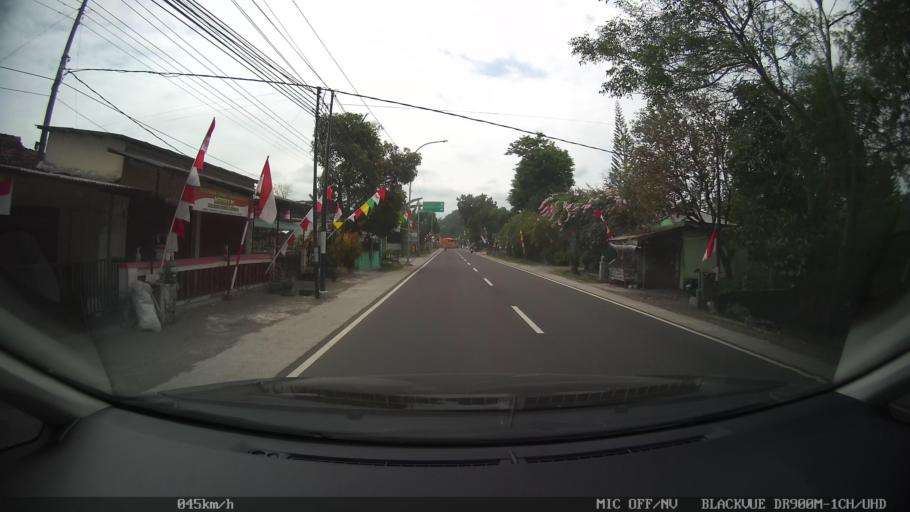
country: ID
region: Central Java
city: Candi Prambanan
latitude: -7.7833
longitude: 110.4826
